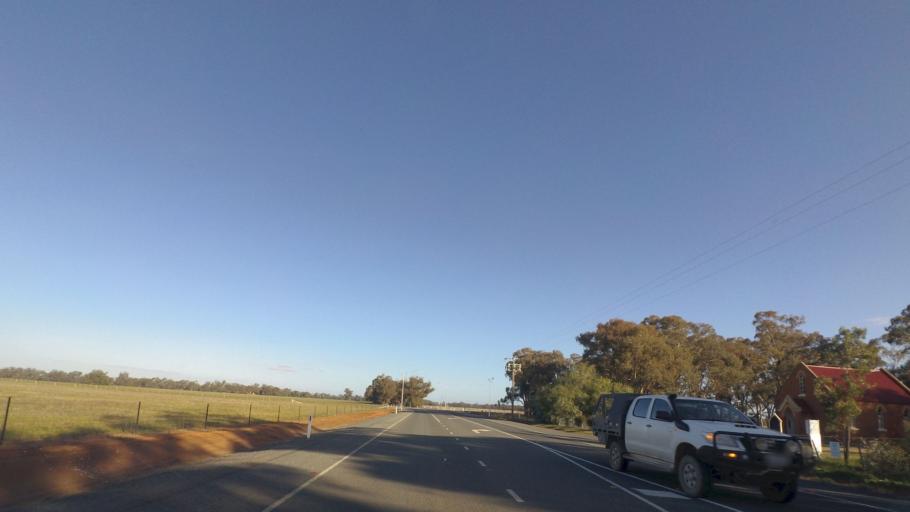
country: AU
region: Victoria
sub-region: Greater Bendigo
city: Epsom
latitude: -36.6513
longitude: 144.5227
